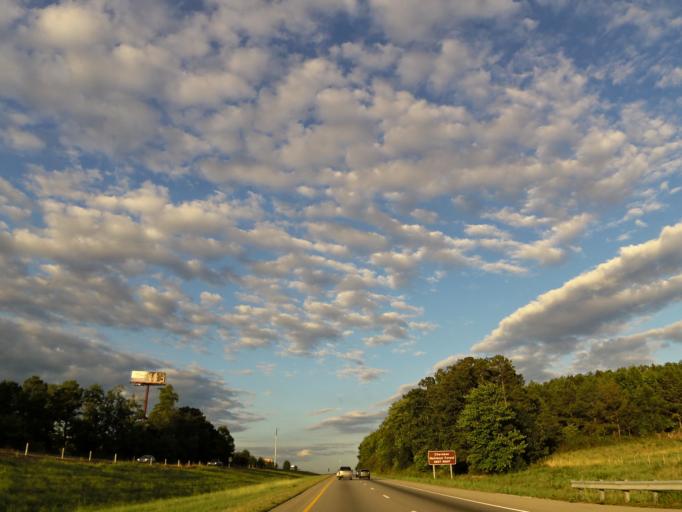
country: US
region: Tennessee
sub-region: Bradley County
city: Cleveland
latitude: 35.1477
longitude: -84.9609
